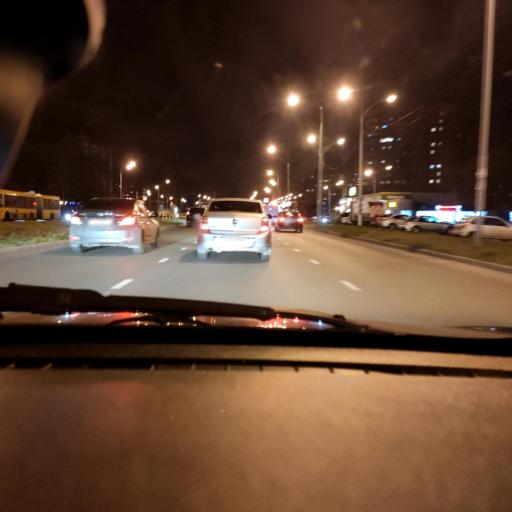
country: RU
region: Samara
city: Tol'yatti
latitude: 53.5391
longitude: 49.3589
